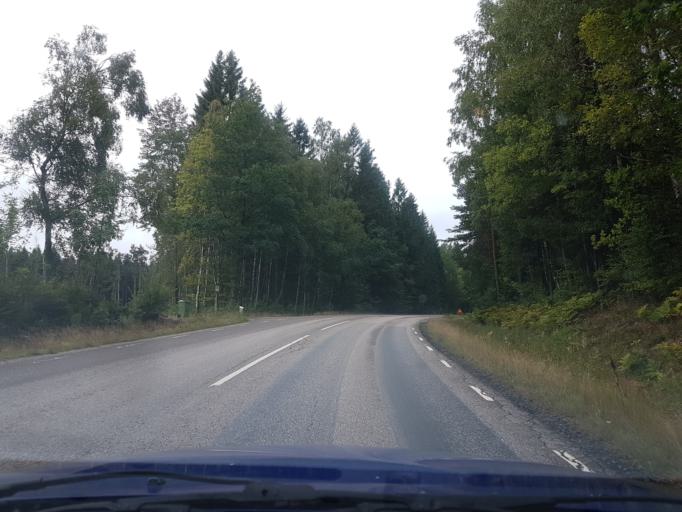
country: SE
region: Vaestra Goetaland
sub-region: Ale Kommun
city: Skepplanda
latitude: 57.9479
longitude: 12.1968
